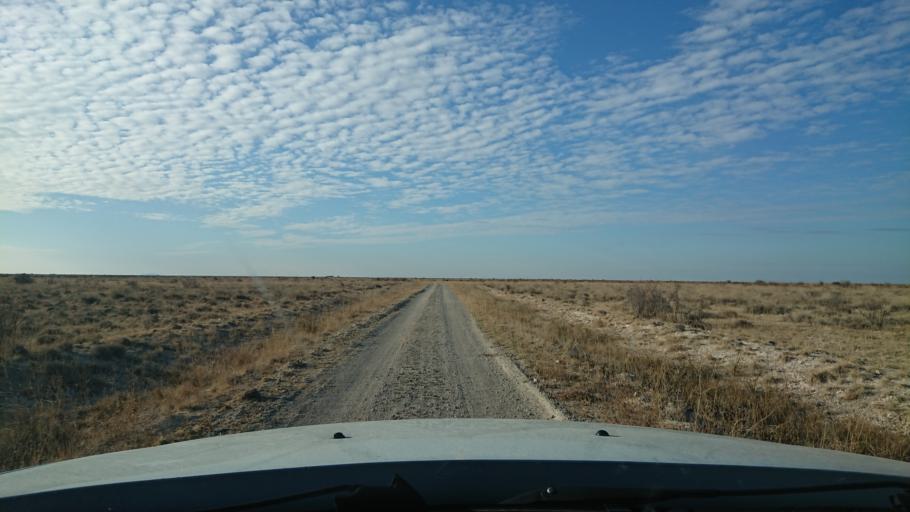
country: TR
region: Aksaray
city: Eskil
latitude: 38.5404
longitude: 33.3378
